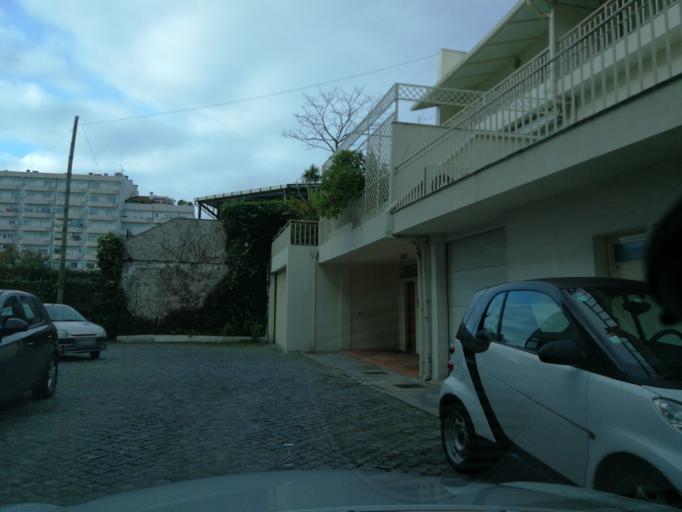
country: PT
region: Braga
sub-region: Braga
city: Braga
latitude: 41.5511
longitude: -8.4092
